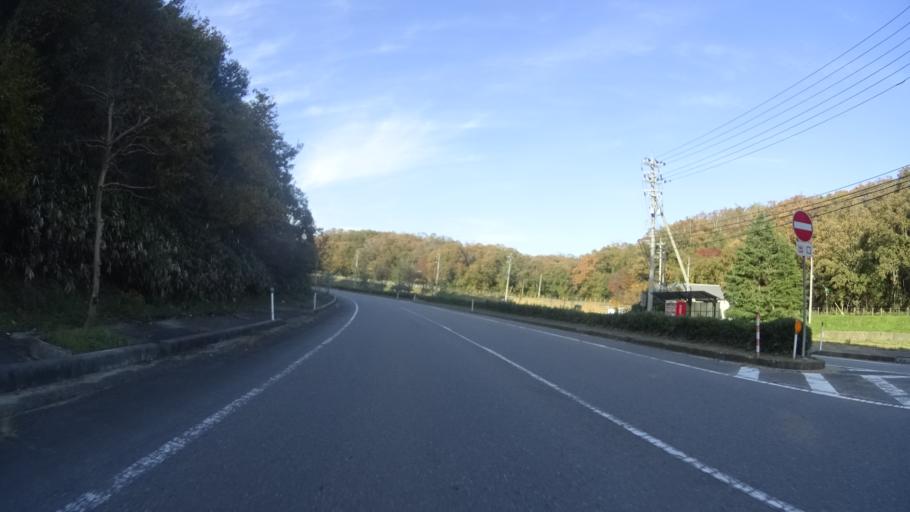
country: JP
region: Ishikawa
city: Hakui
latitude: 37.0306
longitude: 136.7806
